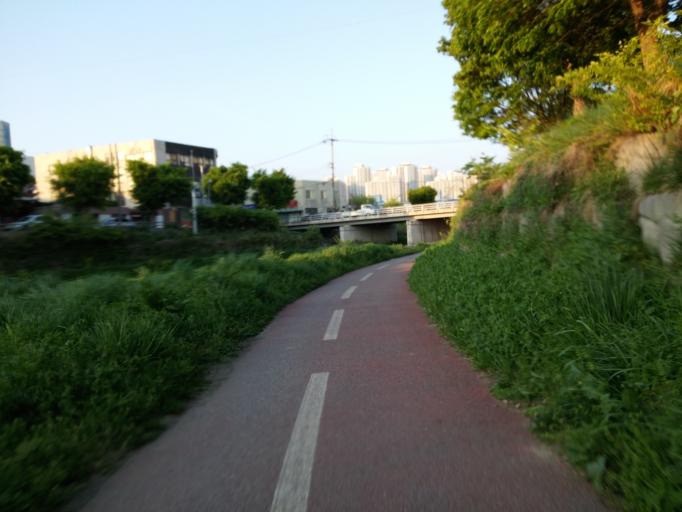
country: KR
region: Daejeon
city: Daejeon
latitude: 36.3388
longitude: 127.4263
